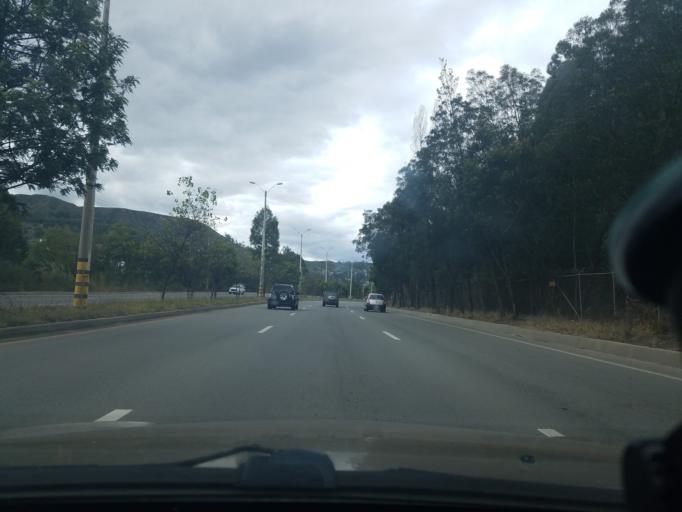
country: EC
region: Azuay
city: Llacao
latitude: -2.8578
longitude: -78.9247
